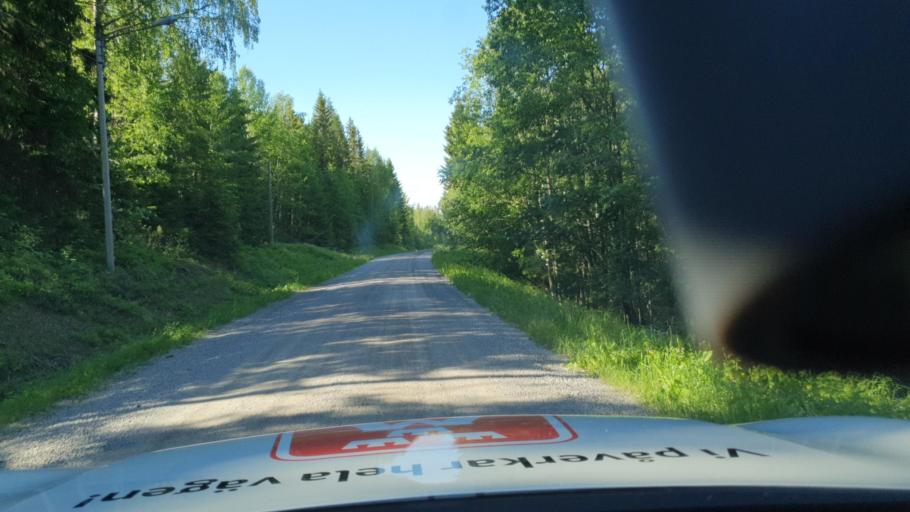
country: SE
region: Vaesterbotten
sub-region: Vannas Kommun
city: Vaennaes
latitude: 63.8171
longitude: 19.6284
